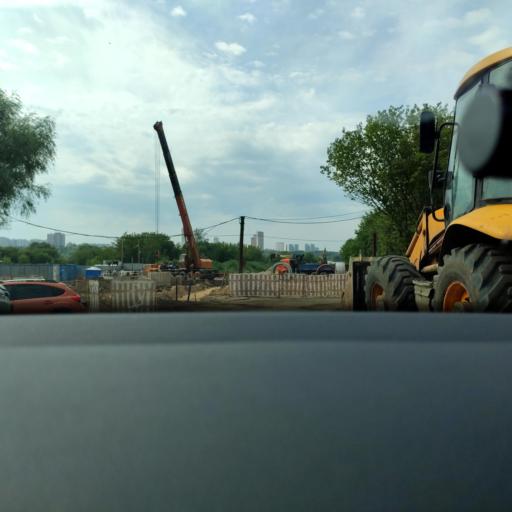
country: RU
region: Moskovskaya
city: Fili
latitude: 55.7466
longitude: 37.4536
